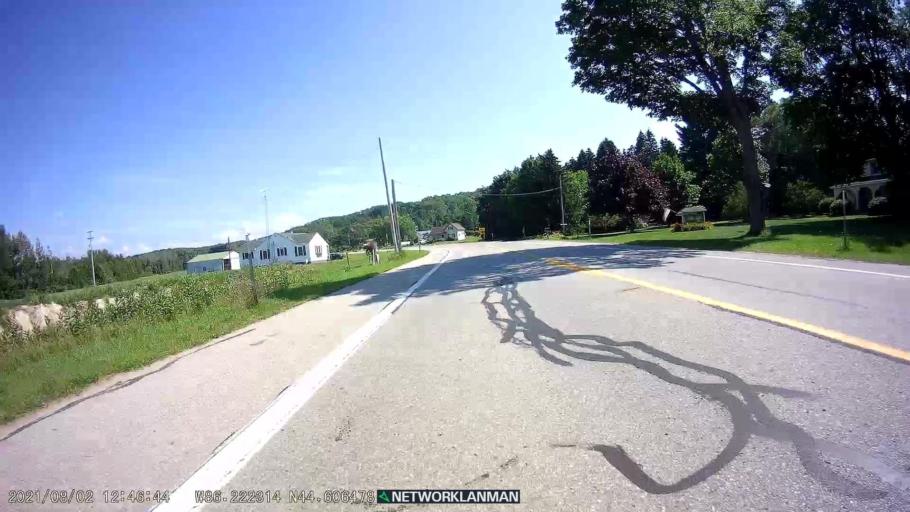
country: US
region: Michigan
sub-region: Benzie County
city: Frankfort
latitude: 44.6066
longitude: -86.2222
